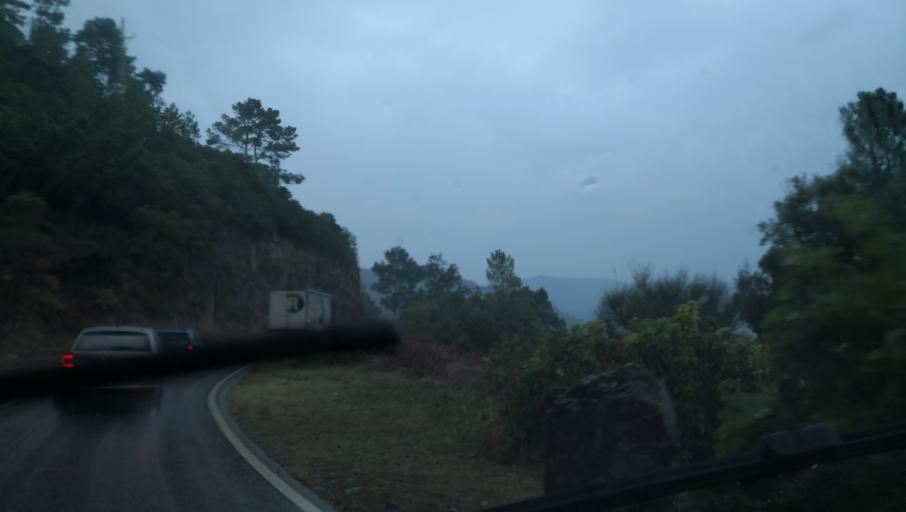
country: PT
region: Vila Real
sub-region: Santa Marta de Penaguiao
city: Santa Marta de Penaguiao
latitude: 41.2145
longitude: -7.7288
